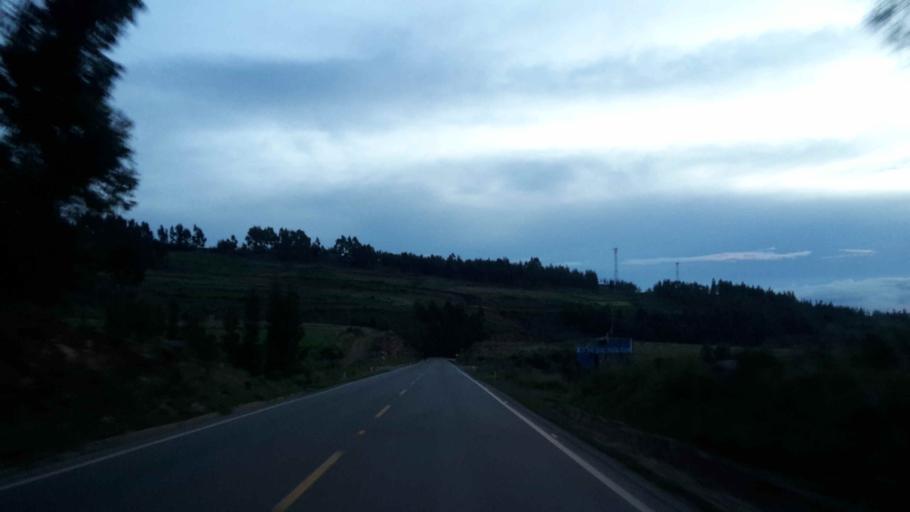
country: BO
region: Cochabamba
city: Colomi
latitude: -17.4202
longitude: -65.8992
